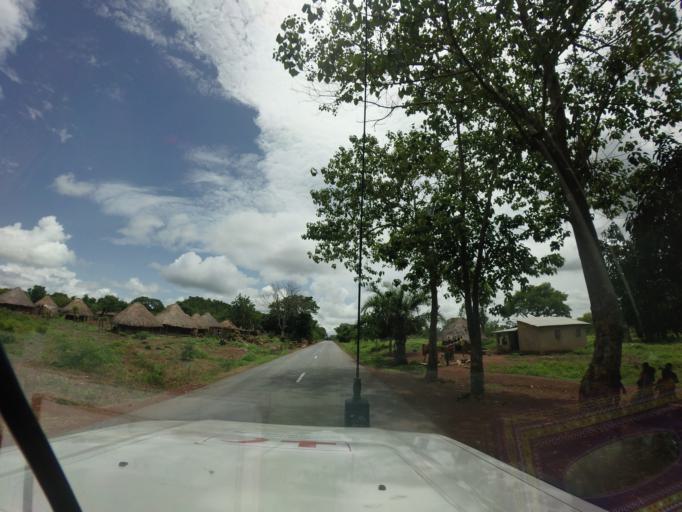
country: SL
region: Northern Province
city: Gberia Fotombu
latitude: 10.0639
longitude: -11.0384
